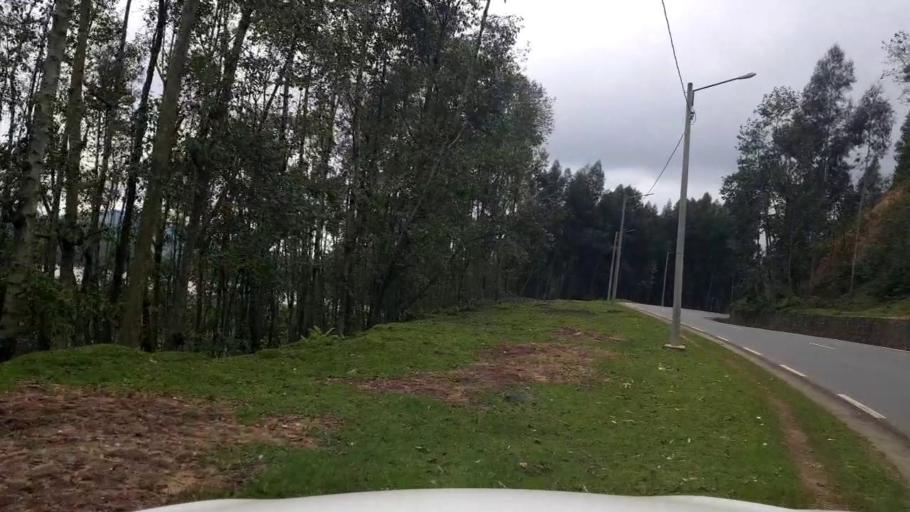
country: RW
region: Northern Province
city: Musanze
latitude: -1.6226
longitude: 29.5050
